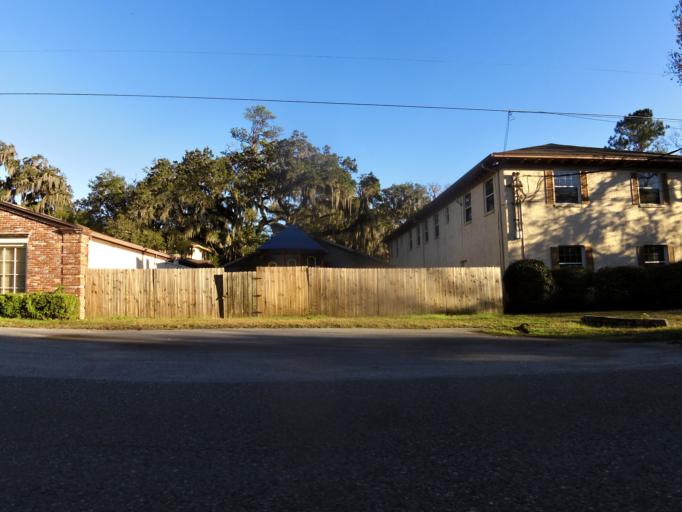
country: US
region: Florida
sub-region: Duval County
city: Jacksonville
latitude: 30.2730
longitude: -81.7043
